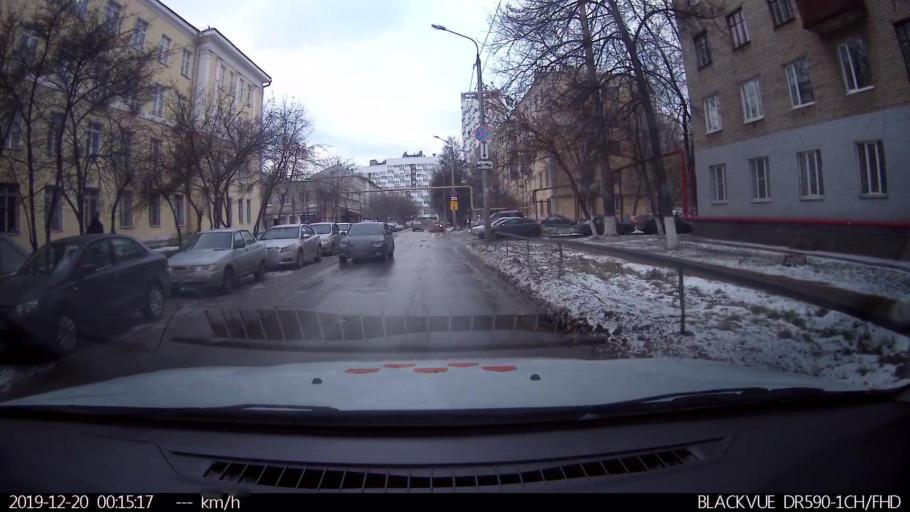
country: RU
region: Jaroslavl
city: Porech'ye-Rybnoye
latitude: 56.9952
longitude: 39.3868
